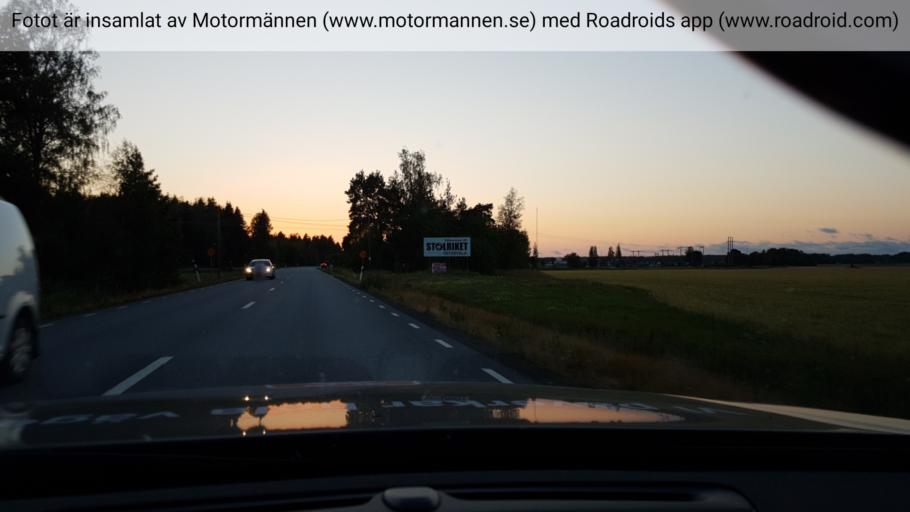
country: SE
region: Uppsala
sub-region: Heby Kommun
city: OEstervala
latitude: 60.1645
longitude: 17.1972
